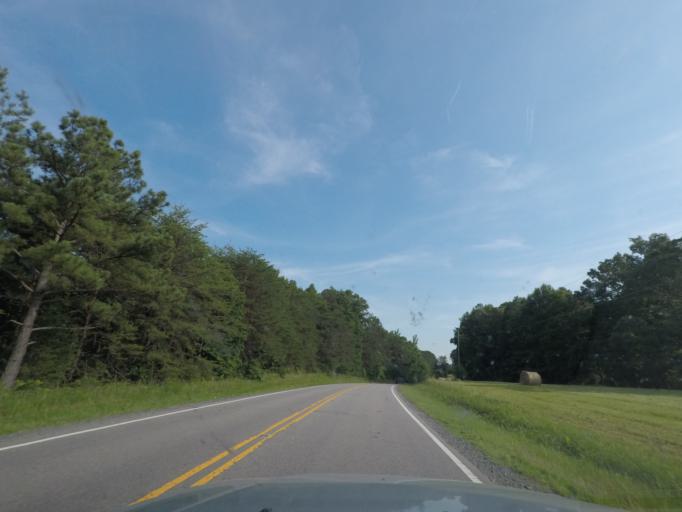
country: US
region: Virginia
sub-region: Mecklenburg County
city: Clarksville
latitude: 36.5160
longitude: -78.5341
